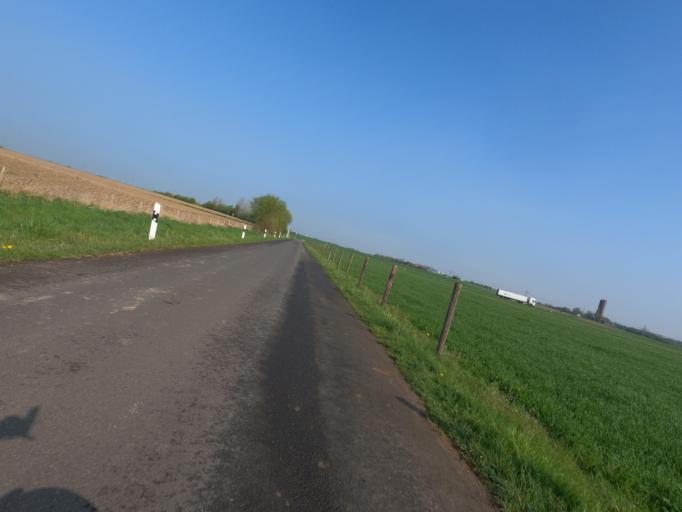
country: DE
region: North Rhine-Westphalia
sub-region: Regierungsbezirk Koln
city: Heinsberg
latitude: 51.0354
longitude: 6.1279
